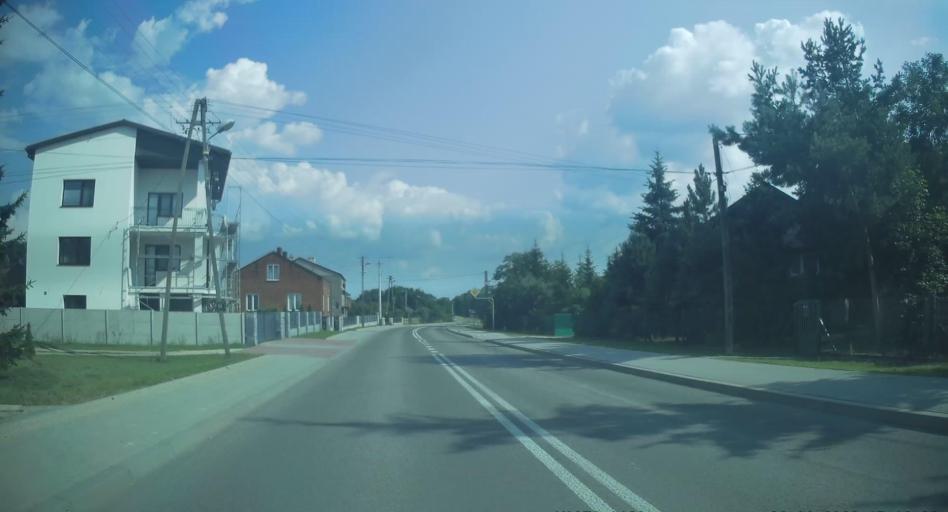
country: PL
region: Swietokrzyskie
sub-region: Powiat konecki
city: Radoszyce
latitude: 51.0641
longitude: 20.2737
